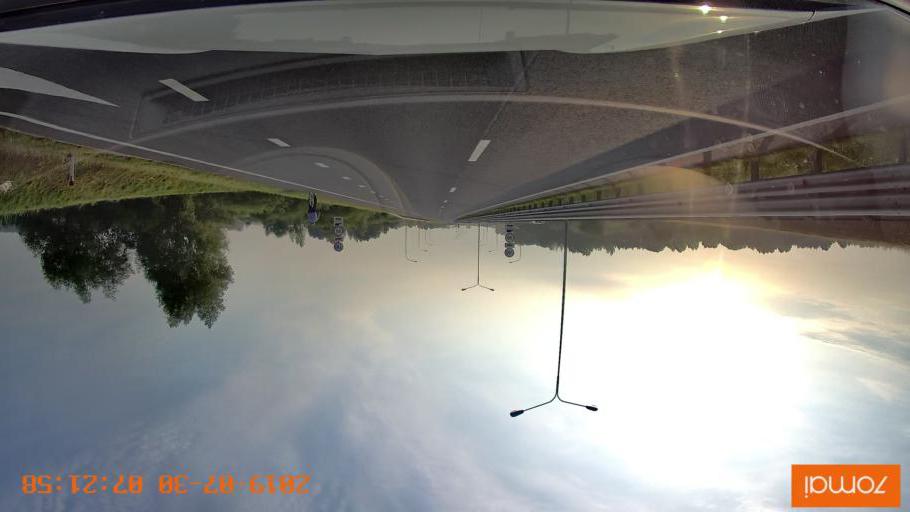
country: RU
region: Kaliningrad
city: Bol'shoe Isakovo
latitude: 54.6941
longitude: 20.7430
